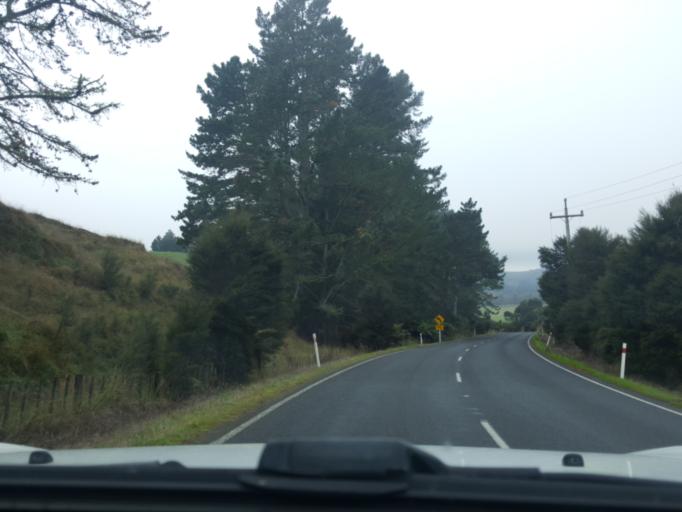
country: NZ
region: Auckland
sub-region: Auckland
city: Pukekohe East
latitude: -37.2872
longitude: 175.0387
